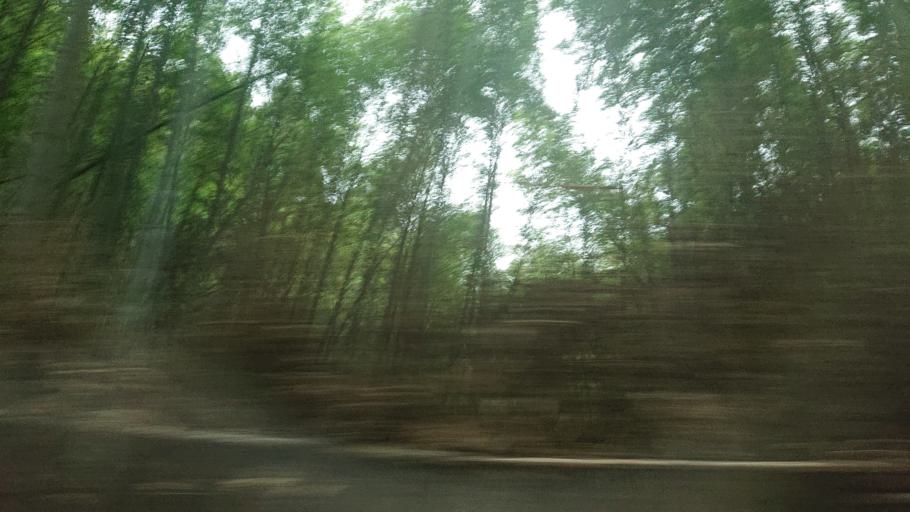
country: TW
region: Taiwan
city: Lugu
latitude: 23.6242
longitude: 120.7132
